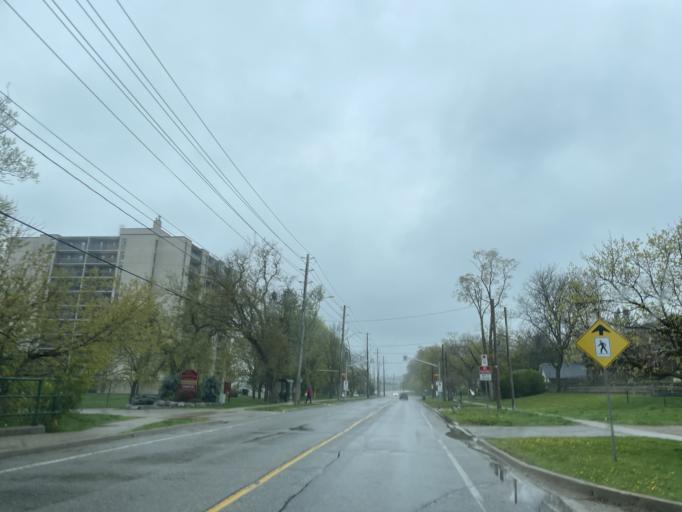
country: CA
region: Ontario
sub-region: Wellington County
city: Guelph
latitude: 43.5316
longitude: -80.2603
